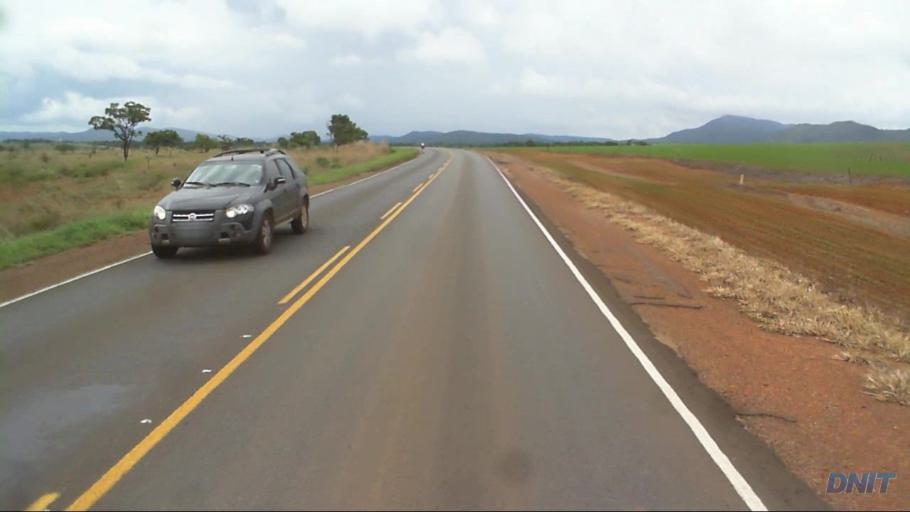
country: BR
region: Goias
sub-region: Padre Bernardo
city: Padre Bernardo
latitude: -15.3388
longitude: -48.2341
